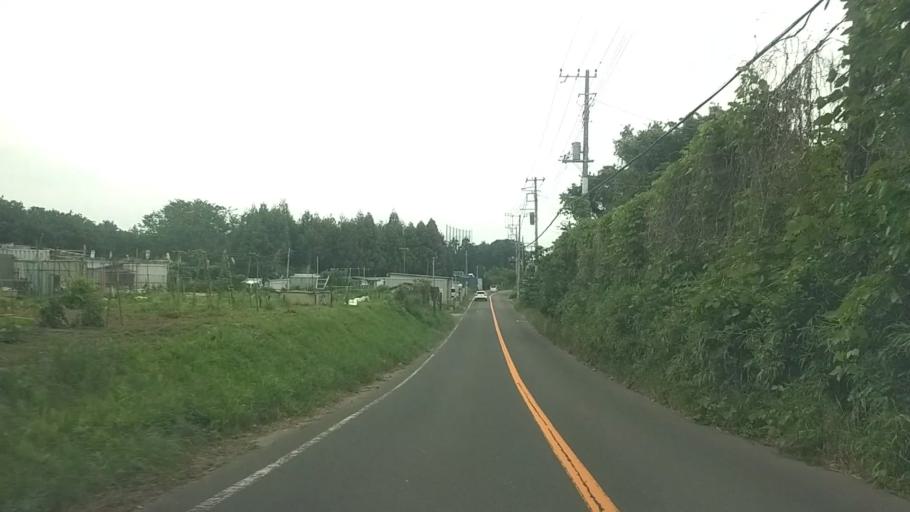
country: JP
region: Kanagawa
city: Fujisawa
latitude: 35.3545
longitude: 139.4352
